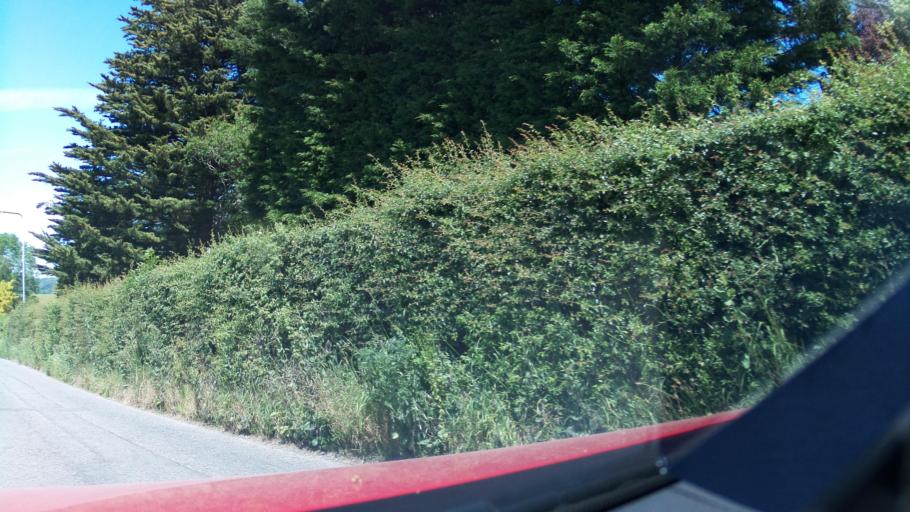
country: GB
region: Wales
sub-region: Monmouthshire
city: Caldicot
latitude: 51.5951
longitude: -2.7316
